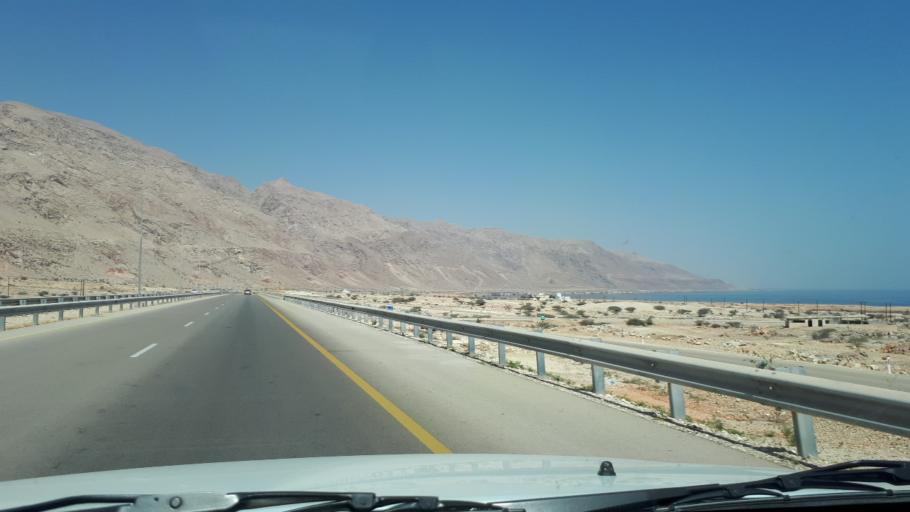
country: OM
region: Ash Sharqiyah
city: Sur
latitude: 22.7460
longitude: 59.3235
